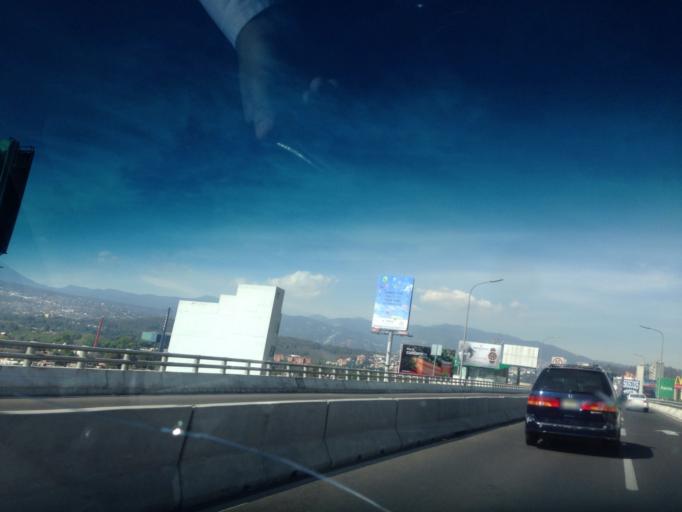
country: MX
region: Mexico City
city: Tlalpan
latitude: 19.3030
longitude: -99.1740
